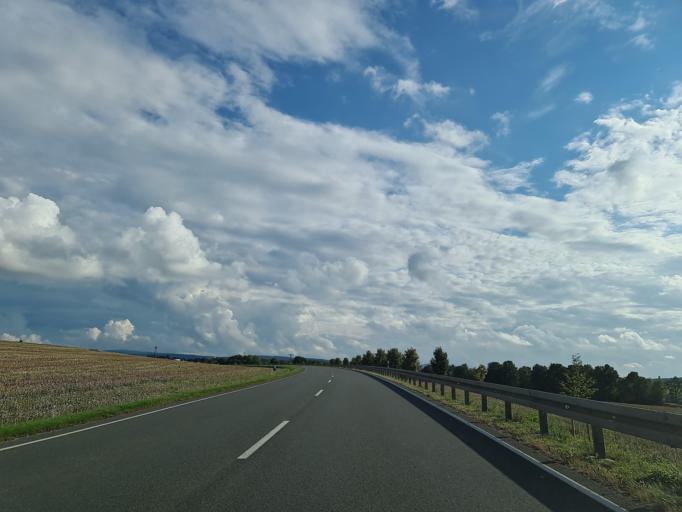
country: DE
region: Saxony
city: Auerbach
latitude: 50.5320
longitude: 12.3746
